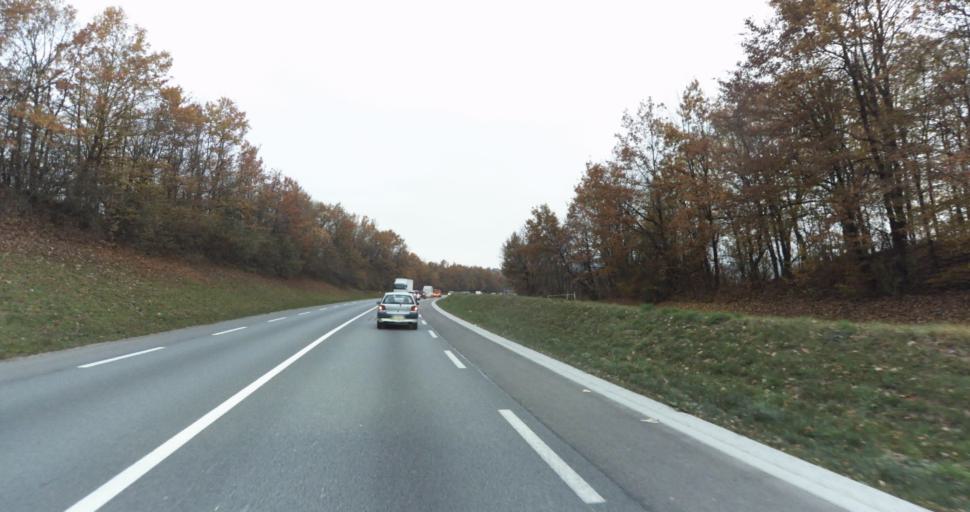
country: FR
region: Rhone-Alpes
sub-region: Departement de la Haute-Savoie
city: Meythet
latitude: 45.9094
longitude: 6.0844
